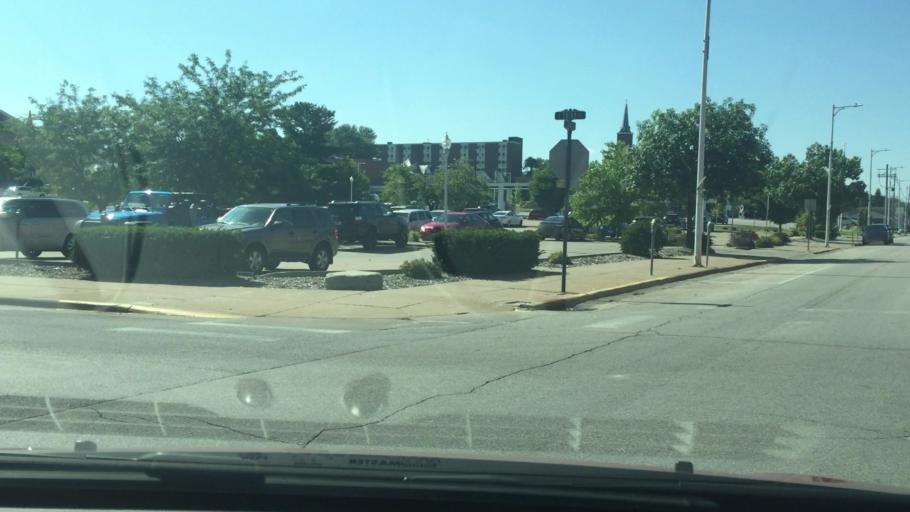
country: US
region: Iowa
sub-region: Muscatine County
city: Muscatine
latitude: 41.4233
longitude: -91.0443
